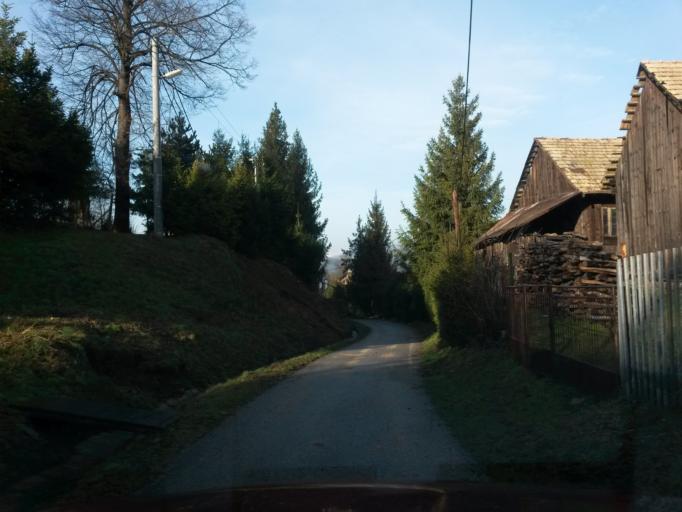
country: SK
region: Kosicky
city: Roznava
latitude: 48.7112
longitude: 20.4345
